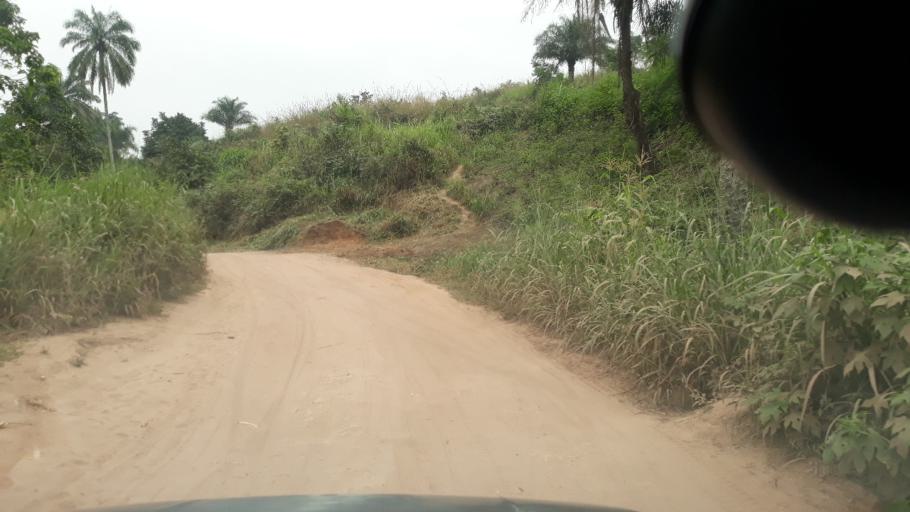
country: CD
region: Bas-Congo
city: Kasangulu
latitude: -4.4785
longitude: 15.2727
